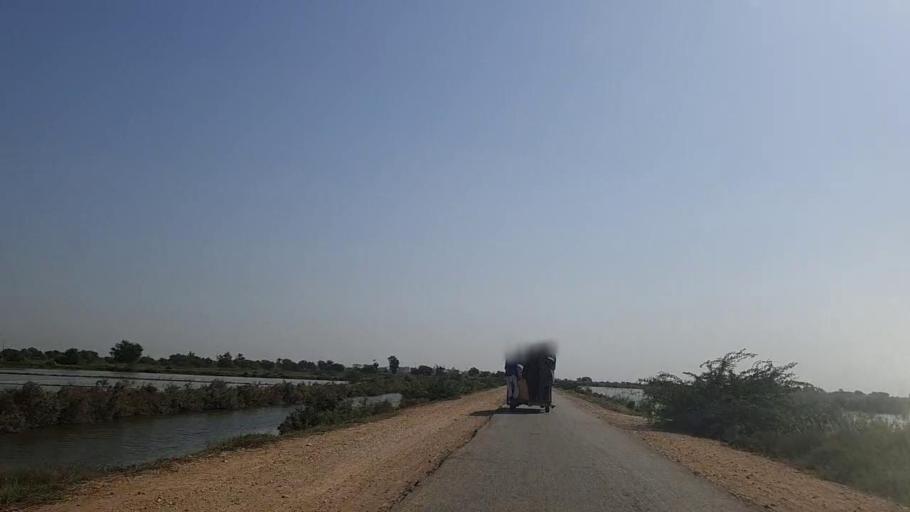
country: PK
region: Sindh
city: Mirpur Batoro
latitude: 24.6505
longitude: 68.2885
